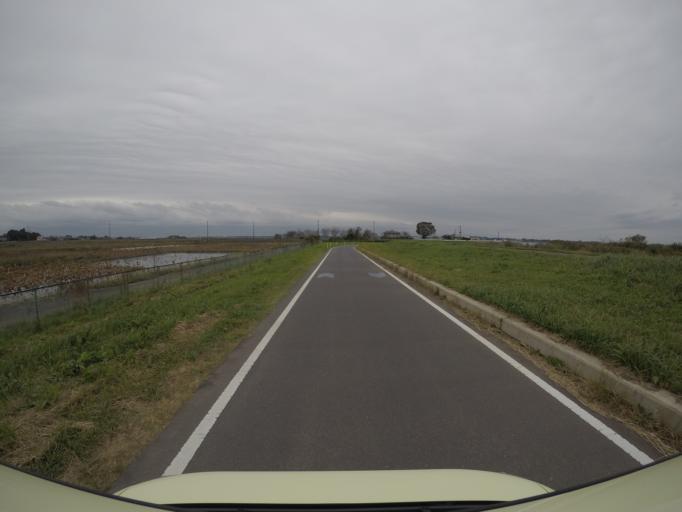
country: JP
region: Ibaraki
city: Ami
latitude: 36.0744
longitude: 140.2415
